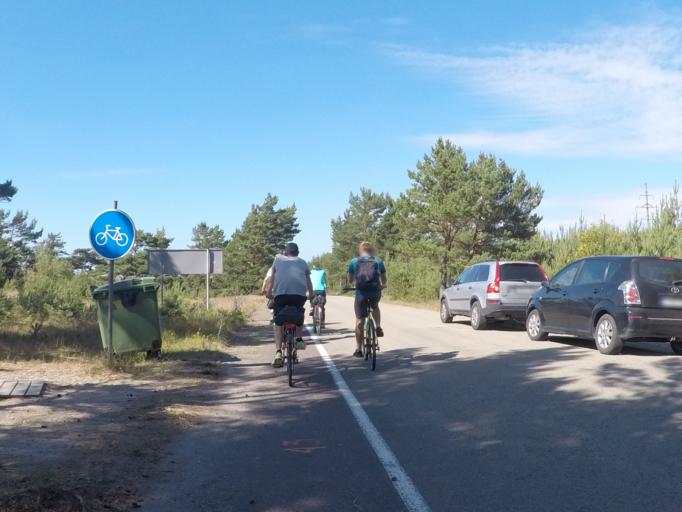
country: LT
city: Neringa
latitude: 55.5277
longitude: 21.0976
